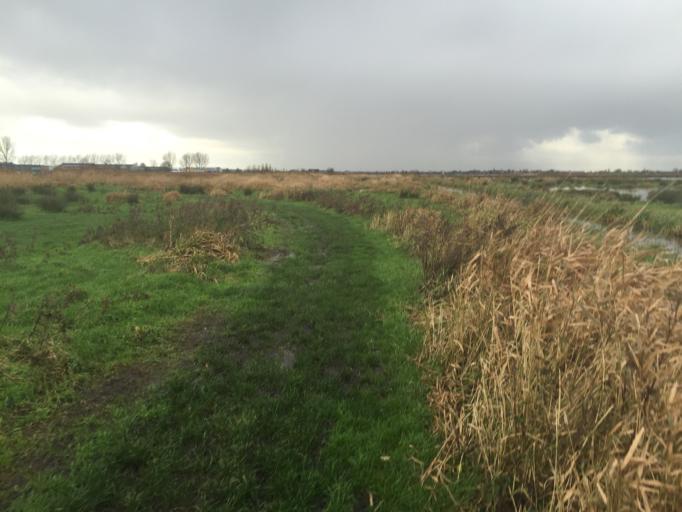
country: NL
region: South Holland
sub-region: Gemeente Nieuwkoop
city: Nieuwkoop
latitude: 52.1582
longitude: 4.7906
